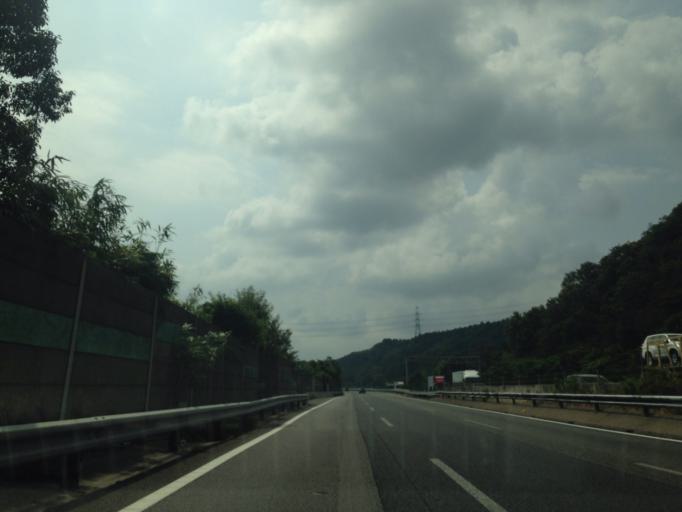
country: JP
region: Aichi
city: Okazaki
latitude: 34.9174
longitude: 137.2384
